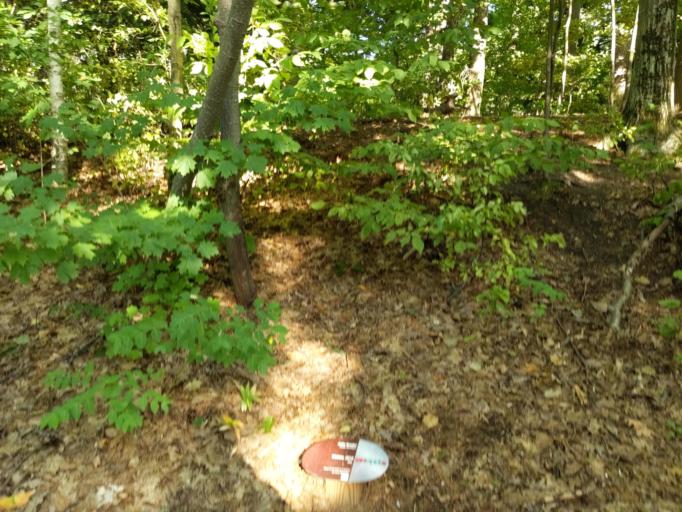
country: US
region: Michigan
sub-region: Antrim County
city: Elk Rapids
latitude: 44.8875
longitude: -85.4230
